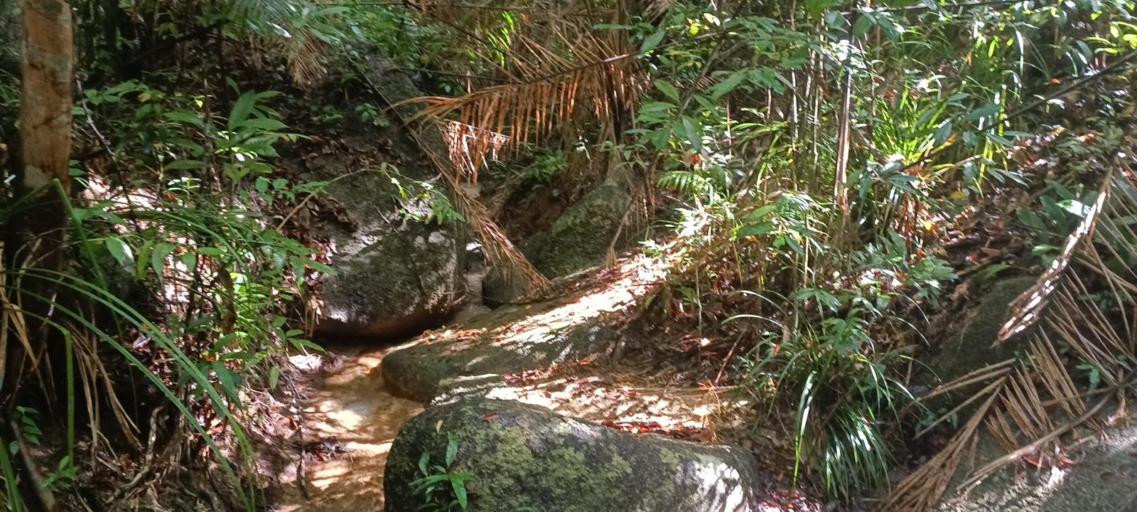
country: MY
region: Penang
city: Tanjung Tokong
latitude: 5.4576
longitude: 100.1934
